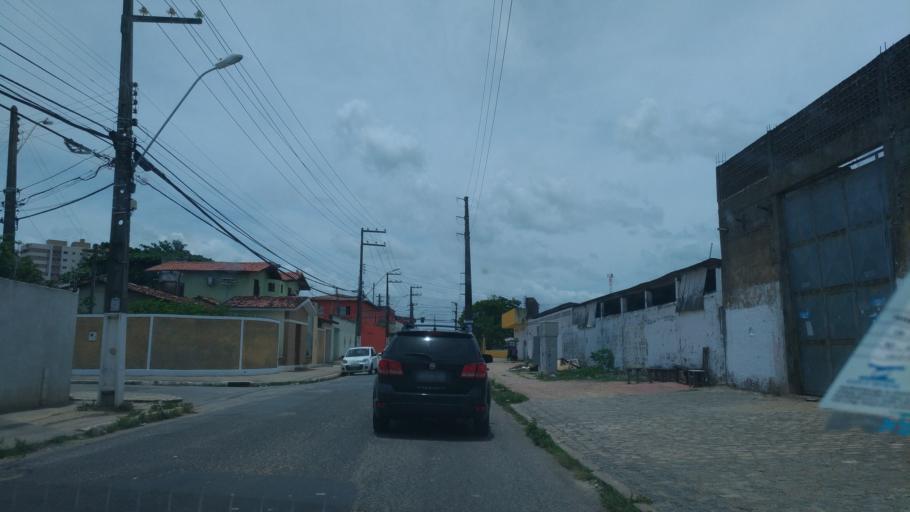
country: BR
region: Alagoas
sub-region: Satuba
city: Satuba
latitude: -9.5651
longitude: -35.7435
